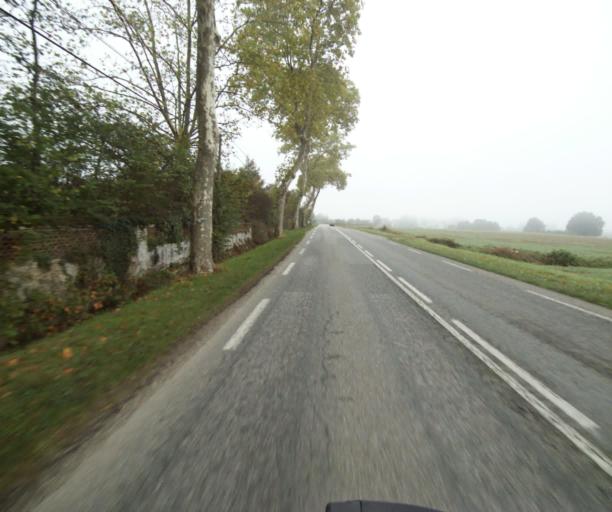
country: FR
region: Midi-Pyrenees
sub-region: Departement du Tarn-et-Garonne
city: Saint-Nauphary
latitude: 43.9461
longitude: 1.4589
